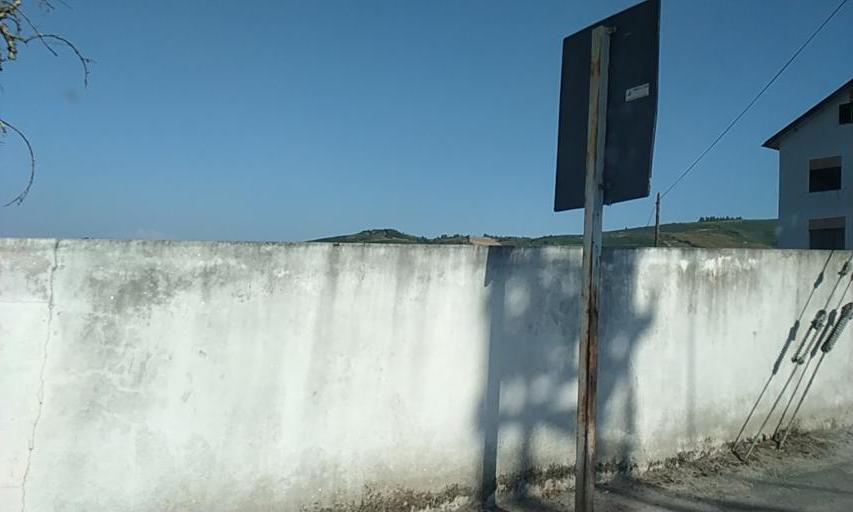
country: PT
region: Viseu
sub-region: Sao Joao da Pesqueira
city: Sao Joao da Pesqueira
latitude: 41.1834
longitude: -7.4154
